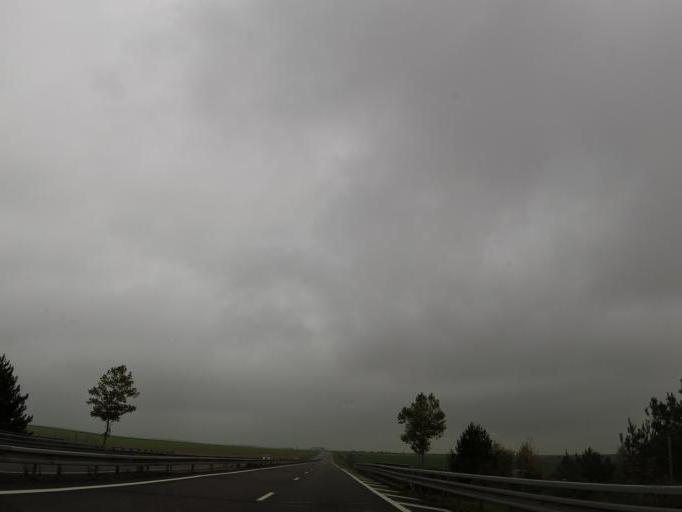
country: FR
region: Champagne-Ardenne
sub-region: Departement de la Marne
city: Courtisols
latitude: 49.0361
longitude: 4.5883
